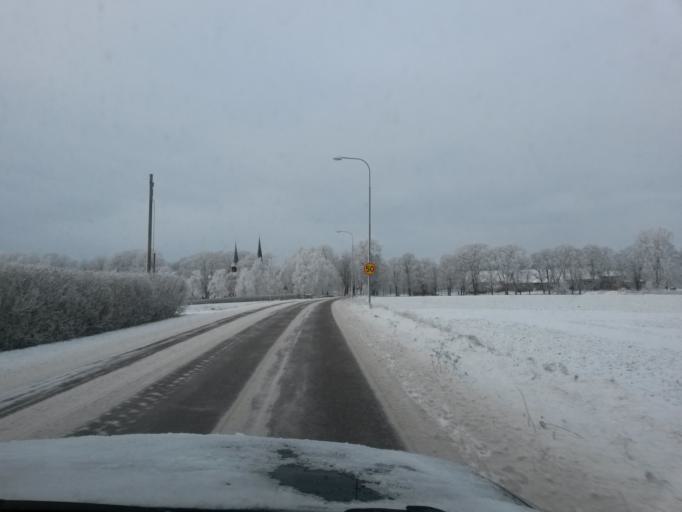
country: SE
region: Vaestra Goetaland
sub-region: Vara Kommun
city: Vara
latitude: 58.3286
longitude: 12.9065
